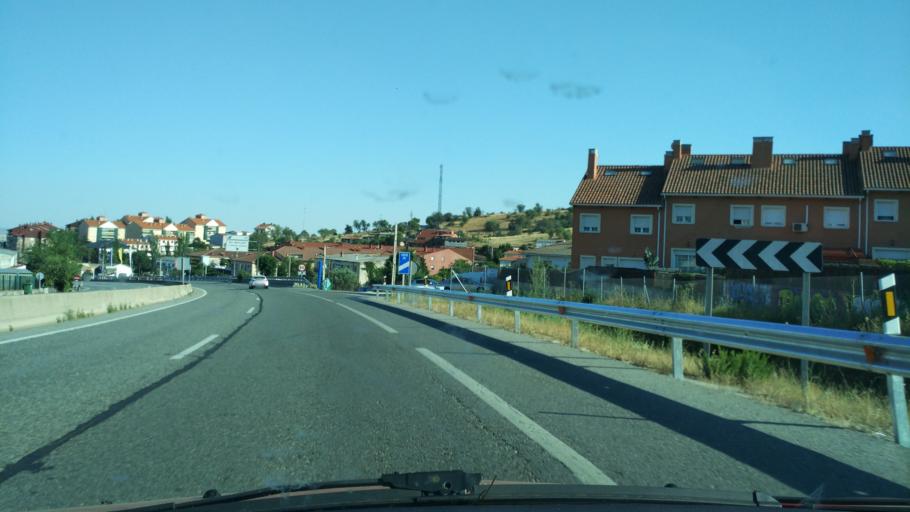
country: ES
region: Madrid
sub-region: Provincia de Madrid
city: El Molar
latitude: 40.7334
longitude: -3.5856
